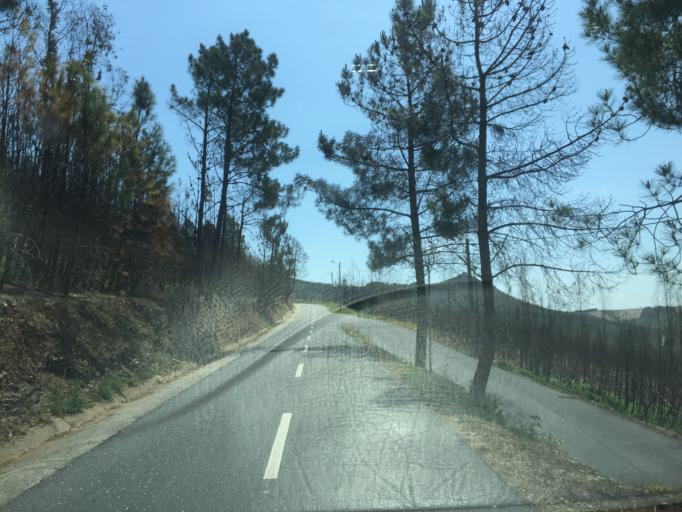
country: PT
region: Coimbra
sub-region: Pampilhosa da Serra
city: Pampilhosa da Serra
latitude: 40.0883
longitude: -7.8760
